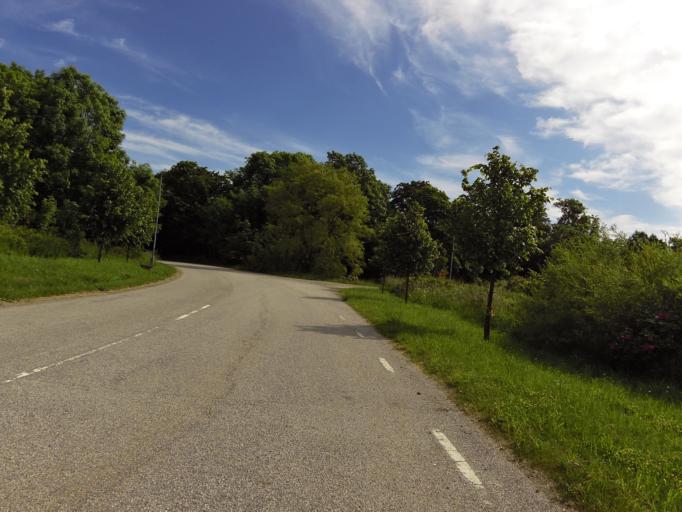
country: SE
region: Skane
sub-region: Staffanstorps Kommun
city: Hjaerup
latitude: 55.6991
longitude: 13.1412
